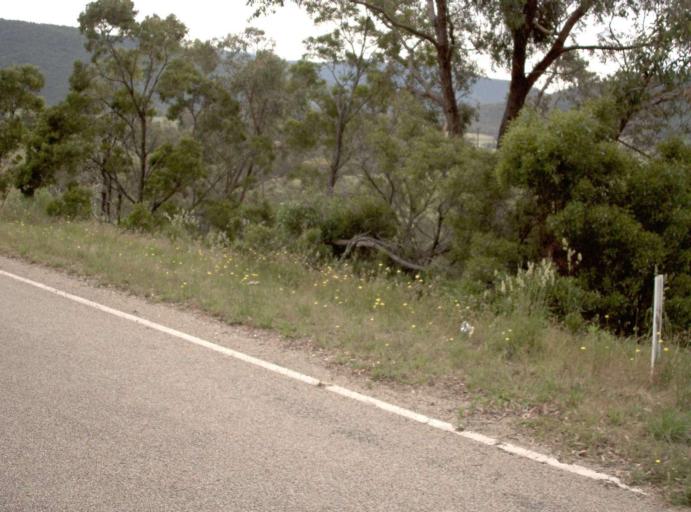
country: AU
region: Victoria
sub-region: East Gippsland
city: Bairnsdale
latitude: -37.5711
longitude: 147.1871
